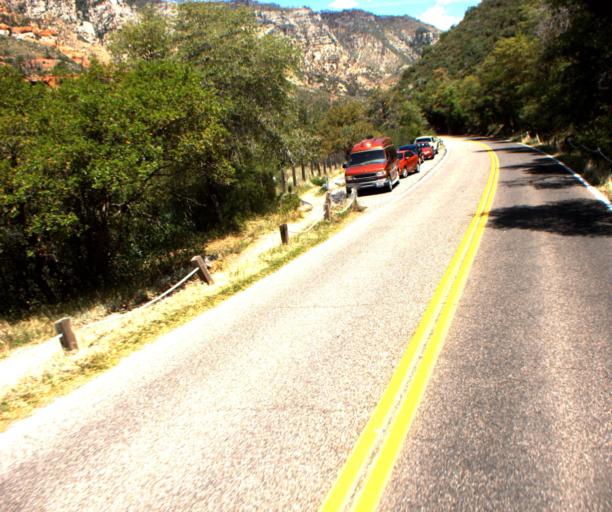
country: US
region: Arizona
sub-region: Coconino County
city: Sedona
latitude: 34.9507
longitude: -111.7537
